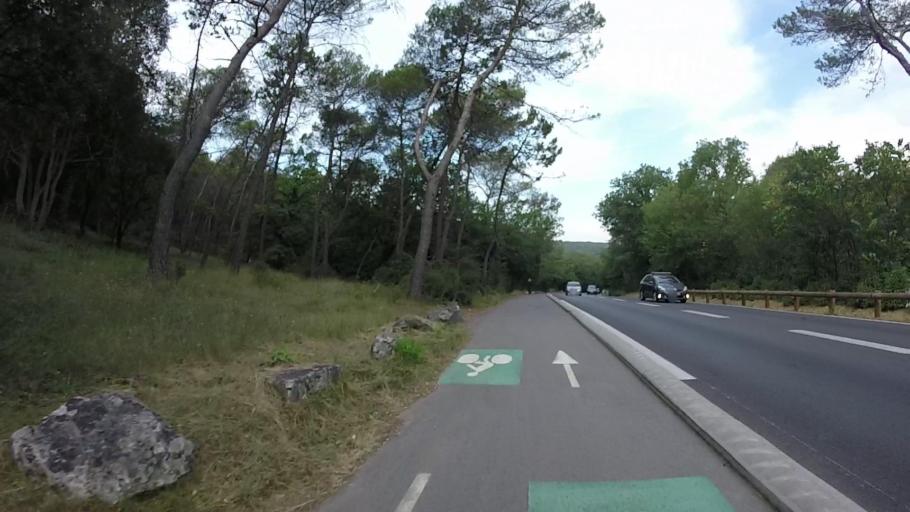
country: FR
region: Provence-Alpes-Cote d'Azur
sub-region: Departement des Alpes-Maritimes
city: Vallauris
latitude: 43.6133
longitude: 7.0454
